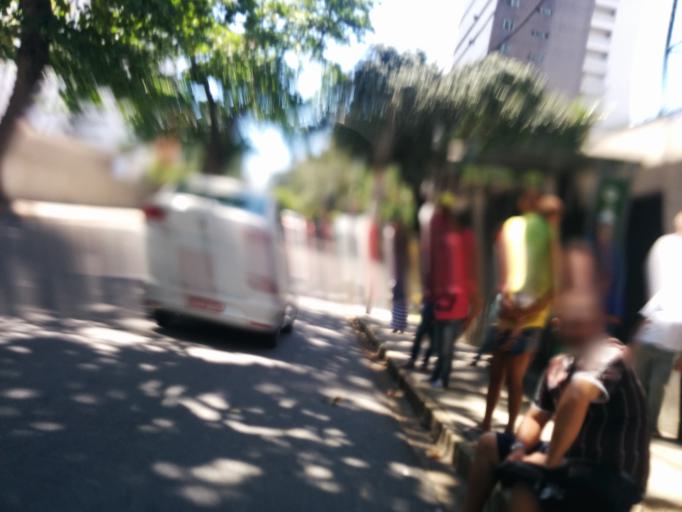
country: BR
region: Pernambuco
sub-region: Recife
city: Recife
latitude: -8.0345
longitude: -34.9053
